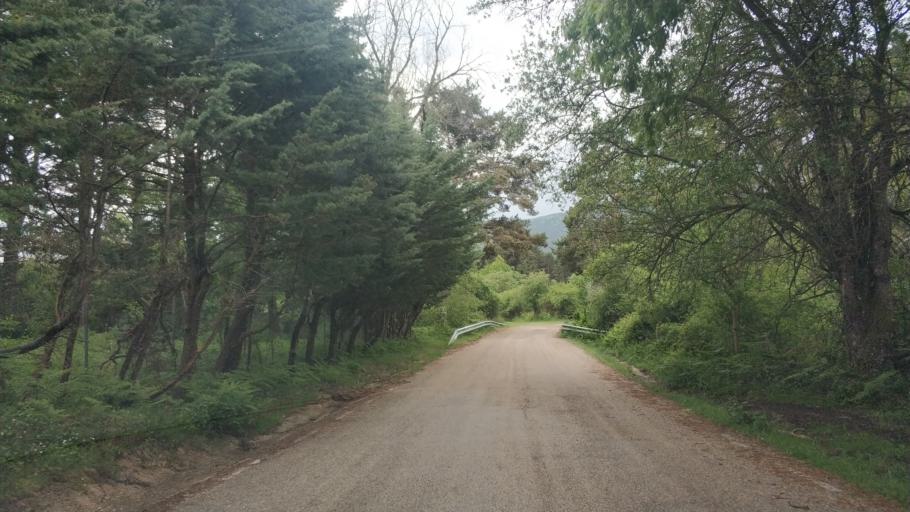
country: ES
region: Castille and Leon
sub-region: Provincia de Soria
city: Vinuesa
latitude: 41.9688
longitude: -2.7810
